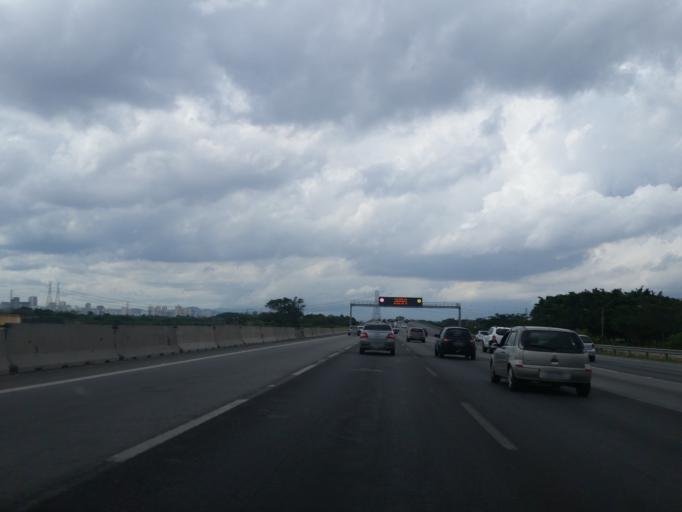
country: BR
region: Sao Paulo
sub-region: Guarulhos
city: Guarulhos
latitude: -23.5025
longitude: -46.5404
